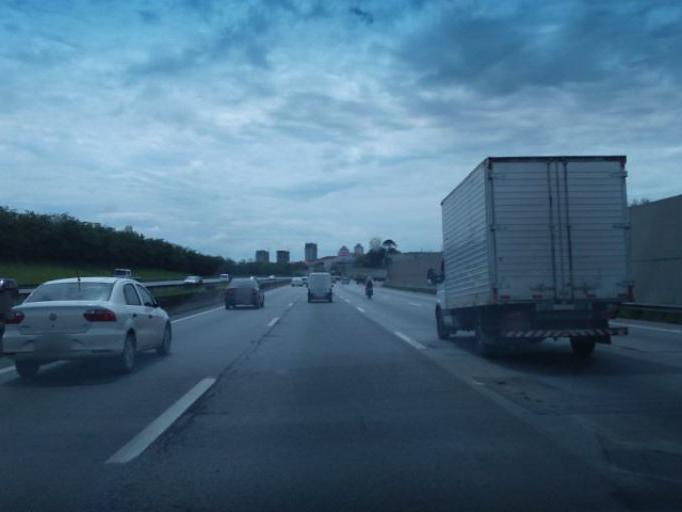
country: BR
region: Sao Paulo
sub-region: Osasco
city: Osasco
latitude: -23.5680
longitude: -46.8163
